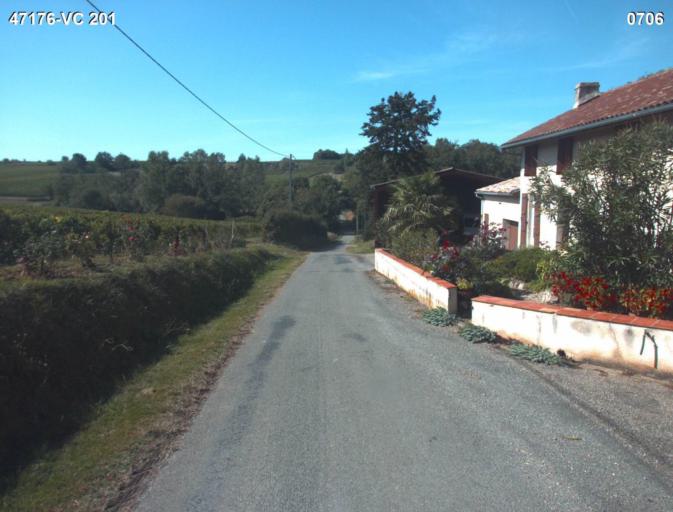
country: FR
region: Aquitaine
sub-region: Departement du Lot-et-Garonne
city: Vianne
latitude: 44.2125
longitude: 0.3059
